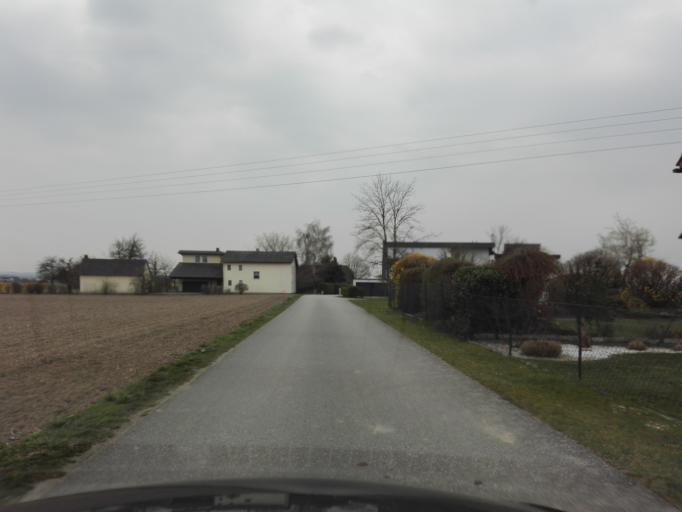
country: AT
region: Upper Austria
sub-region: Politischer Bezirk Perg
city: Perg
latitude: 48.2033
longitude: 14.6717
